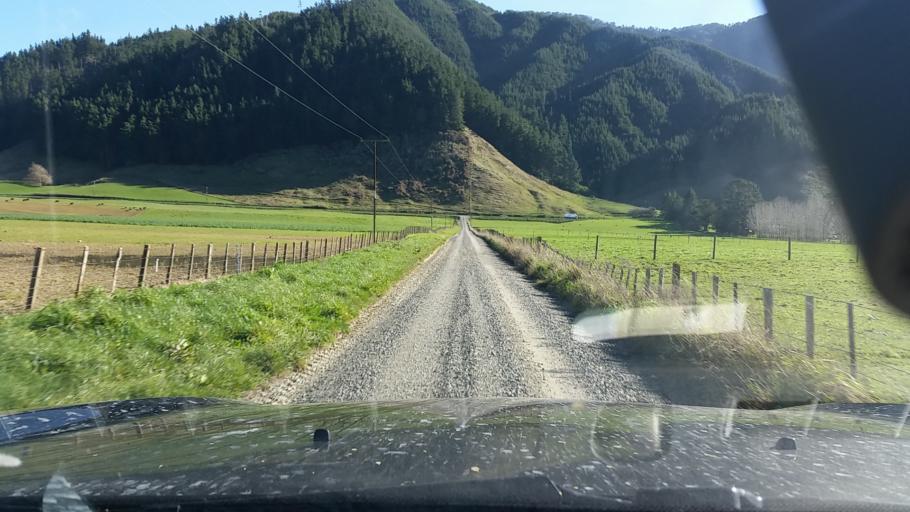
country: NZ
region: Marlborough
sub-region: Marlborough District
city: Picton
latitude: -41.3108
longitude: 173.7731
